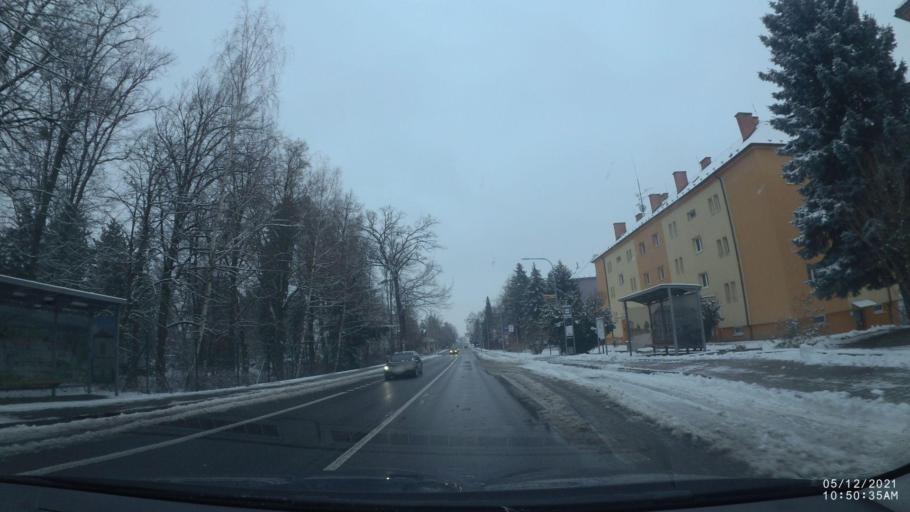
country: CZ
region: Kralovehradecky
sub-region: Okres Rychnov nad Kneznou
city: Rychnov nad Kneznou
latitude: 50.1691
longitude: 16.2694
